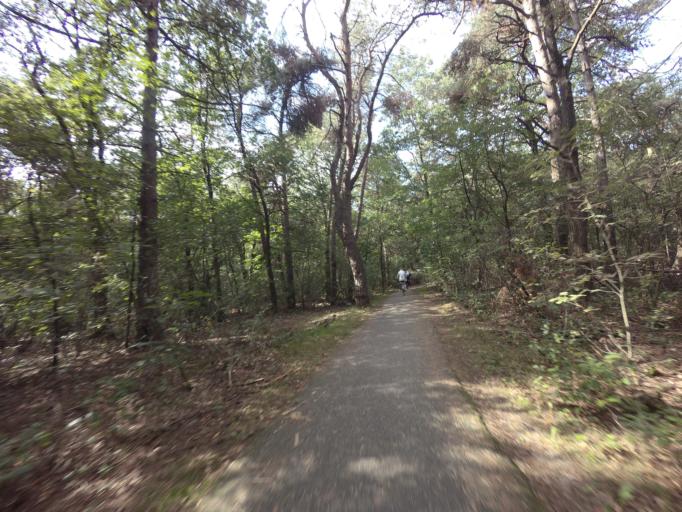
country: NL
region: Drenthe
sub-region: Gemeente De Wolden
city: Ruinen
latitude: 52.7882
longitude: 6.3604
